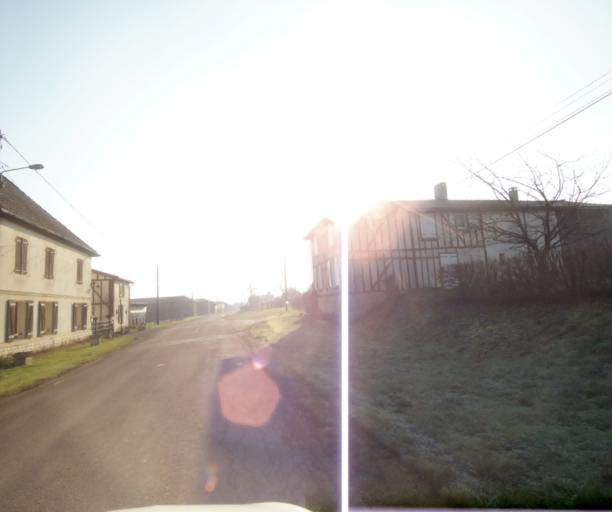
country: FR
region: Champagne-Ardenne
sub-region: Departement de la Haute-Marne
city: Montier-en-Der
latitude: 48.4816
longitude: 4.7499
